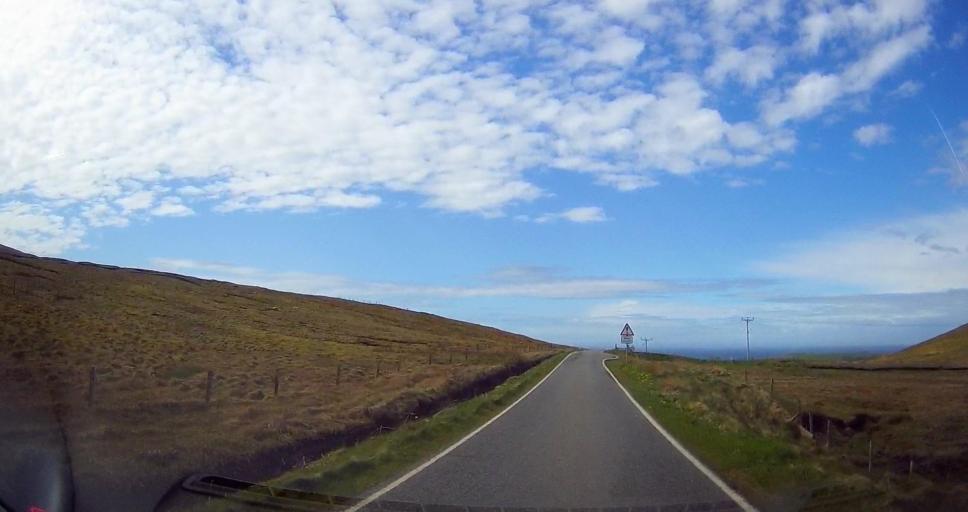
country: GB
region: Scotland
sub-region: Shetland Islands
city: Sandwick
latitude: 59.9801
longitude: -1.2938
